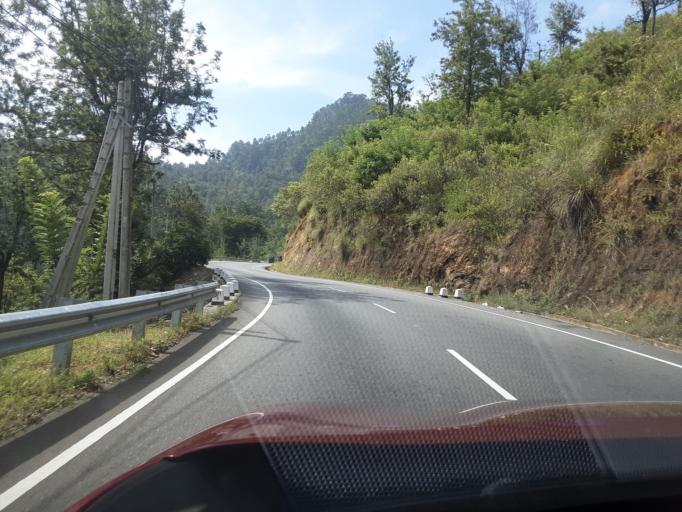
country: LK
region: Uva
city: Badulla
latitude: 6.9603
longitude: 81.1049
